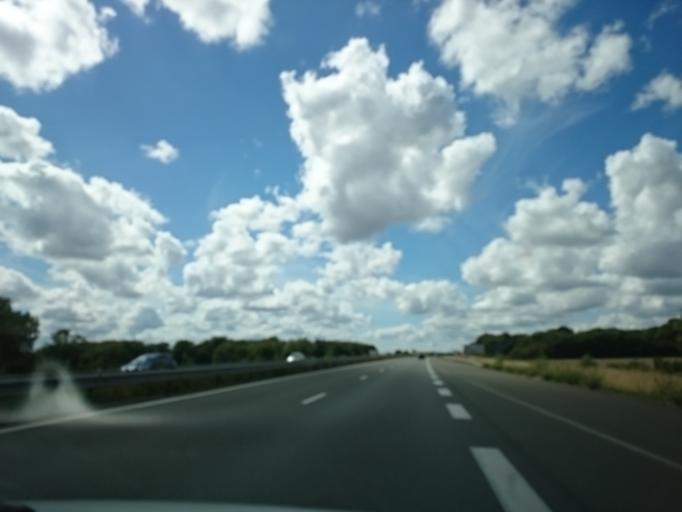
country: FR
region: Pays de la Loire
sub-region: Departement de Maine-et-Loire
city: Saint-Germain-des-Pres
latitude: 47.4339
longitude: -0.7975
